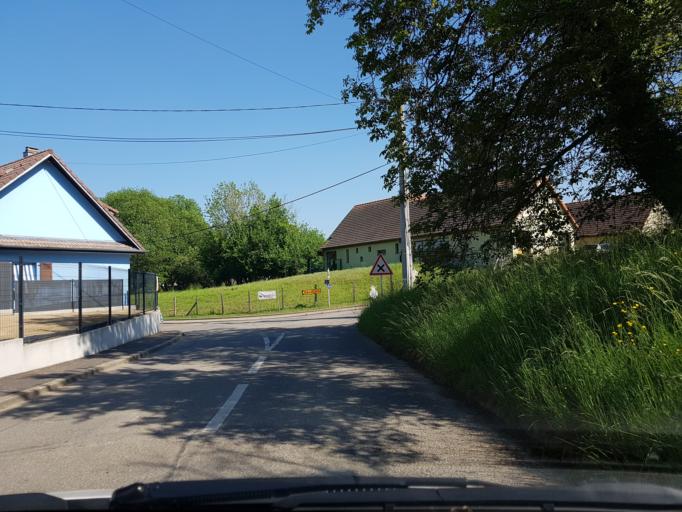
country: FR
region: Alsace
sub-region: Departement du Haut-Rhin
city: Zimmersheim
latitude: 47.7199
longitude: 7.3857
